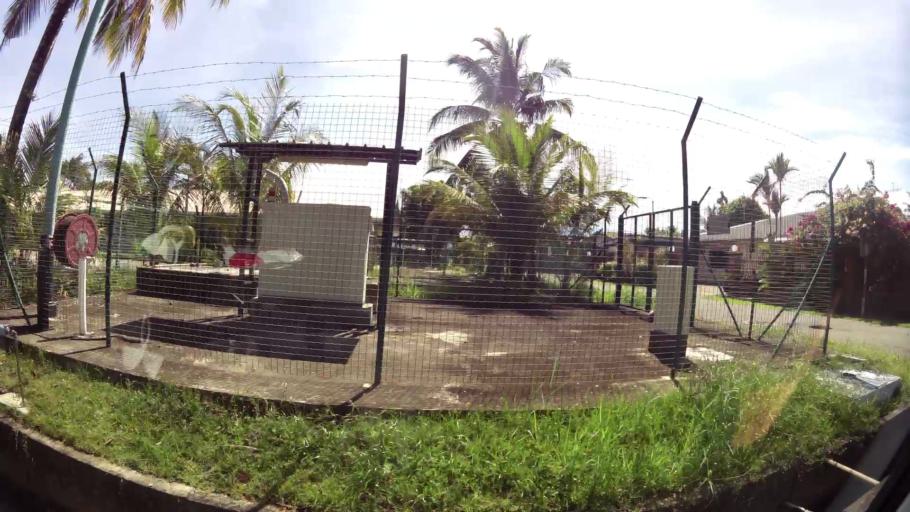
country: BN
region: Belait
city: Kuala Belait
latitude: 4.5899
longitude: 114.2182
